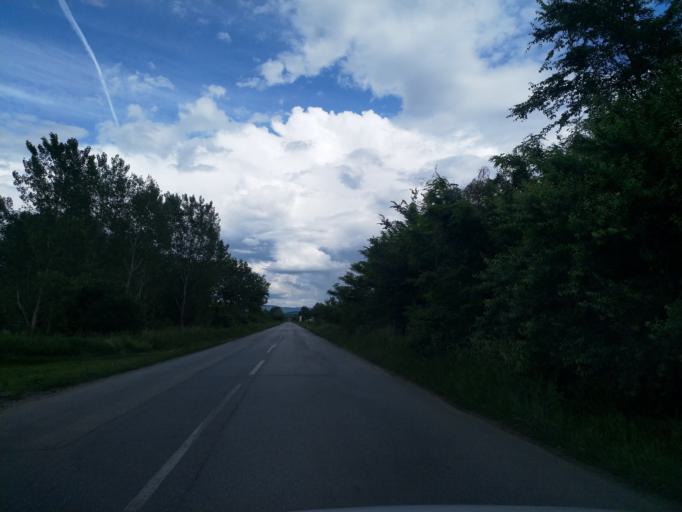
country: RS
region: Central Serbia
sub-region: Pomoravski Okrug
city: Cuprija
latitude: 43.9439
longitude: 21.3471
